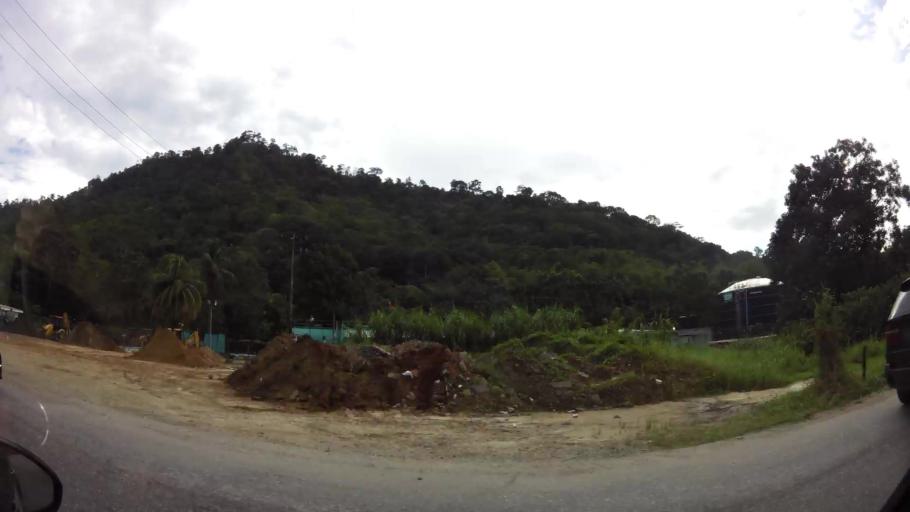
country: TT
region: San Juan/Laventille
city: Laventille
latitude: 10.6854
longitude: -61.4584
